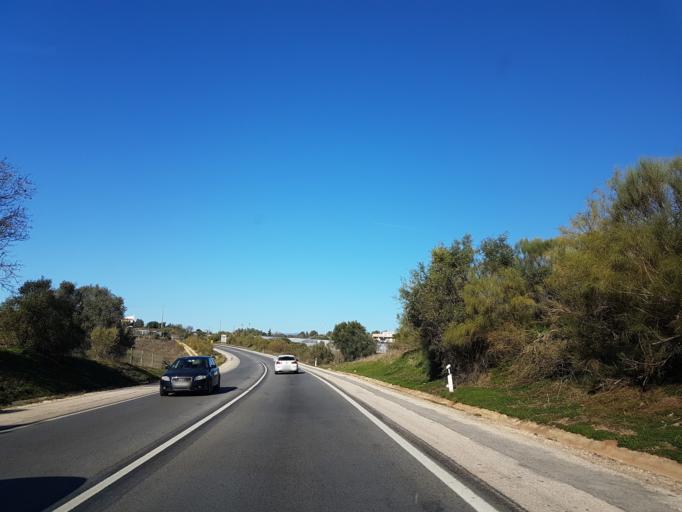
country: PT
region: Faro
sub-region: Lagoa
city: Estombar
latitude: 37.1486
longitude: -8.4792
